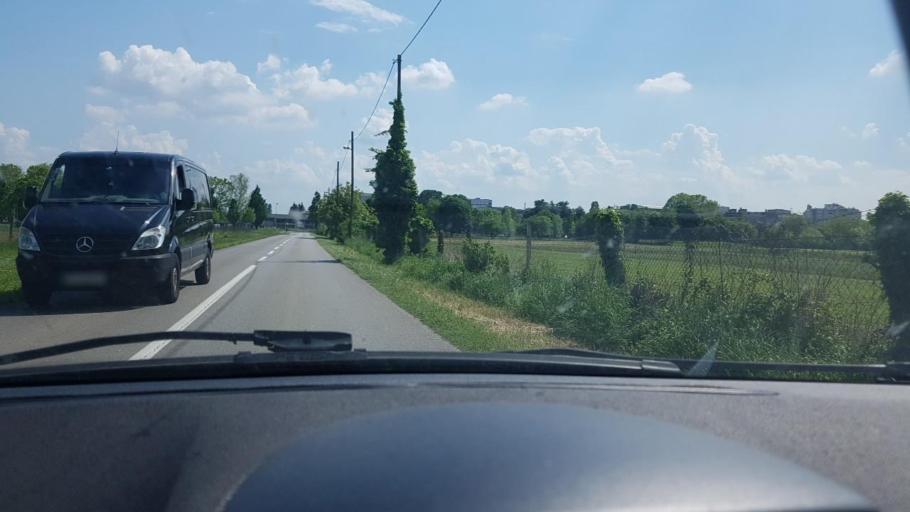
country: HR
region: Grad Zagreb
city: Dubrava
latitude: 45.8257
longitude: 16.0319
